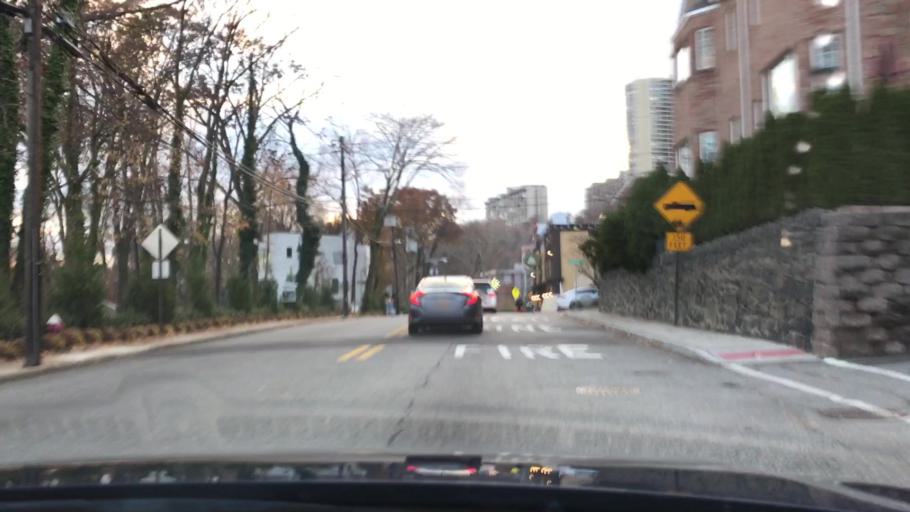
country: US
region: New Jersey
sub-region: Bergen County
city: Fort Lee
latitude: 40.8432
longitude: -73.9681
